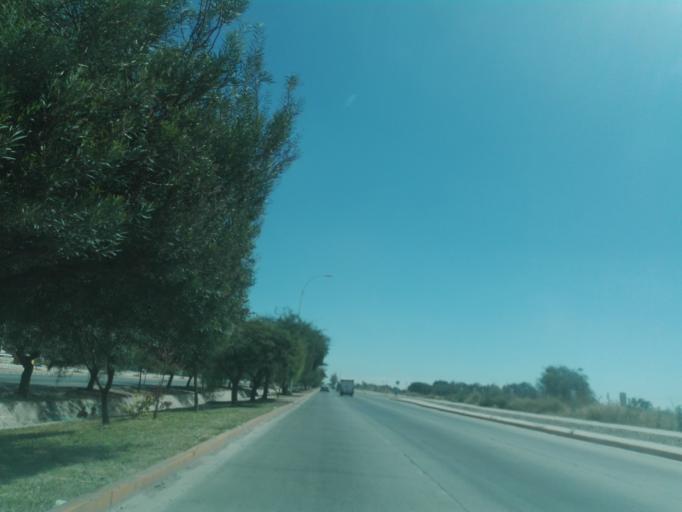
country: MX
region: Guanajuato
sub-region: Leon
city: San Jose de Duran (Los Troncoso)
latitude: 21.0725
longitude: -101.6454
